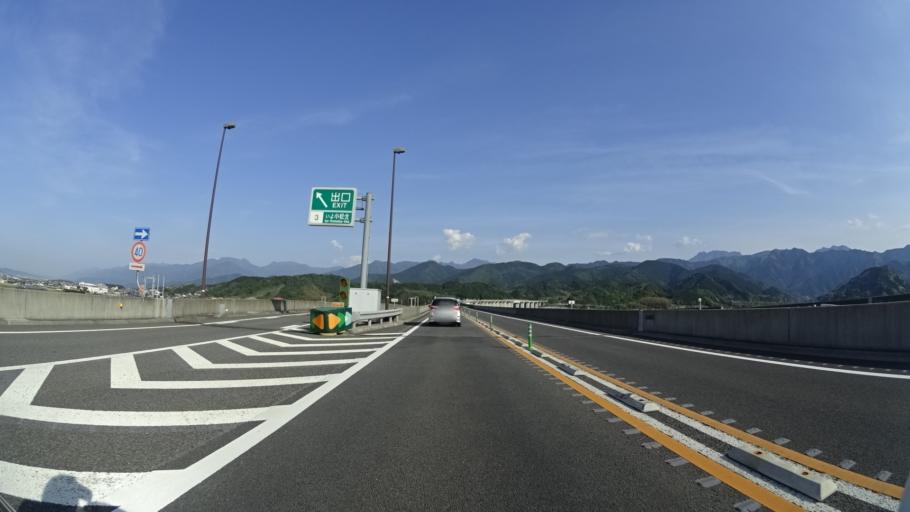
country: JP
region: Ehime
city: Saijo
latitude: 33.8951
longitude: 133.0807
